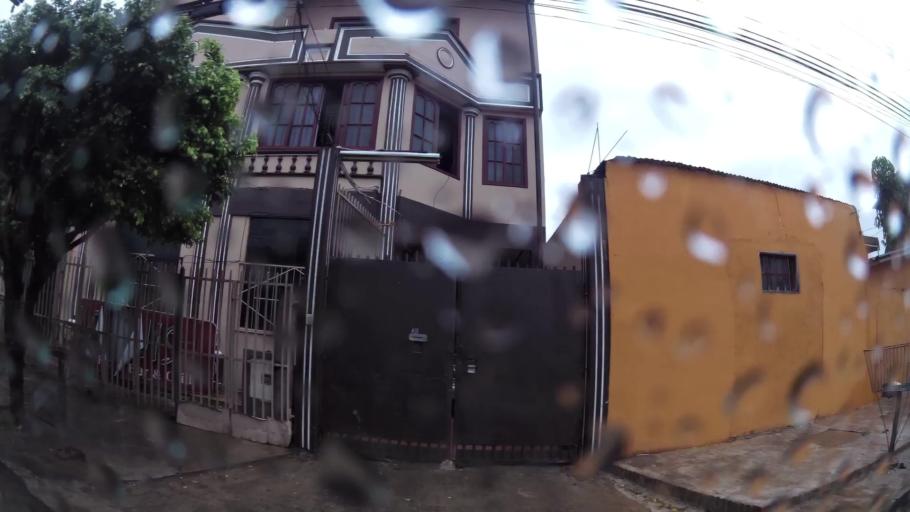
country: BO
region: Santa Cruz
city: Santa Cruz de la Sierra
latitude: -17.7960
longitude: -63.2112
